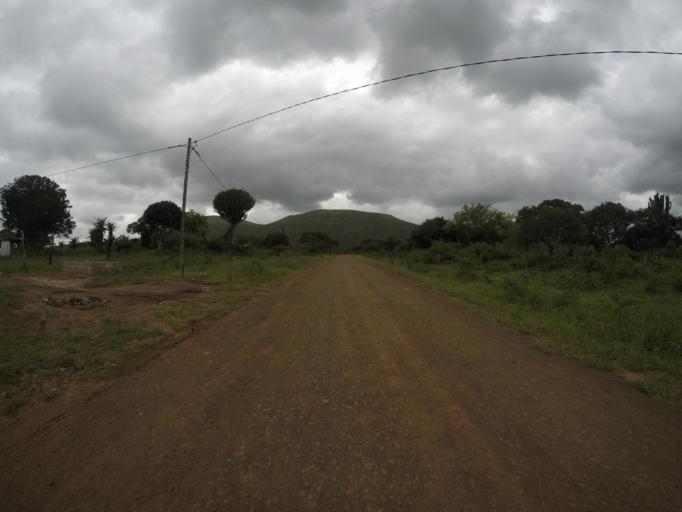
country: ZA
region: KwaZulu-Natal
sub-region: uThungulu District Municipality
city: Empangeni
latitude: -28.5660
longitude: 31.8707
